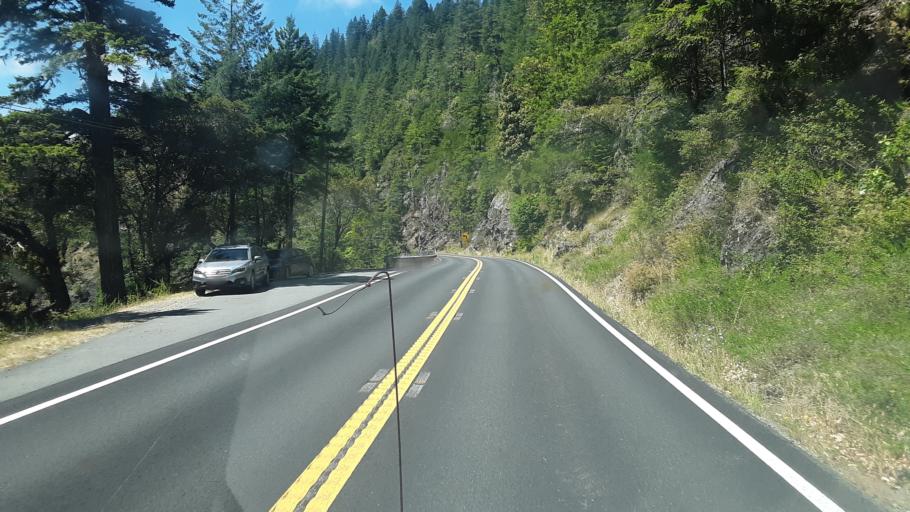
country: US
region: California
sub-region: Del Norte County
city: Bertsch-Oceanview
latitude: 41.8154
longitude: -124.0424
